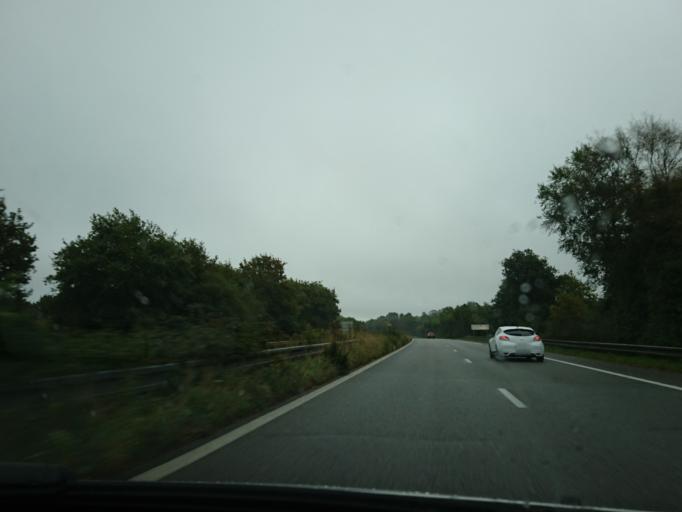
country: FR
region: Brittany
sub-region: Departement du Finistere
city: Quimperle
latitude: 47.8638
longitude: -3.5747
